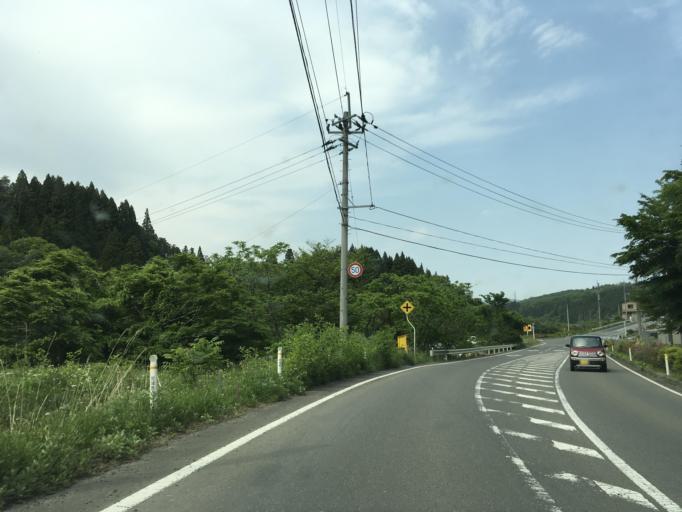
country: JP
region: Iwate
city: Ofunato
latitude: 38.8646
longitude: 141.5284
